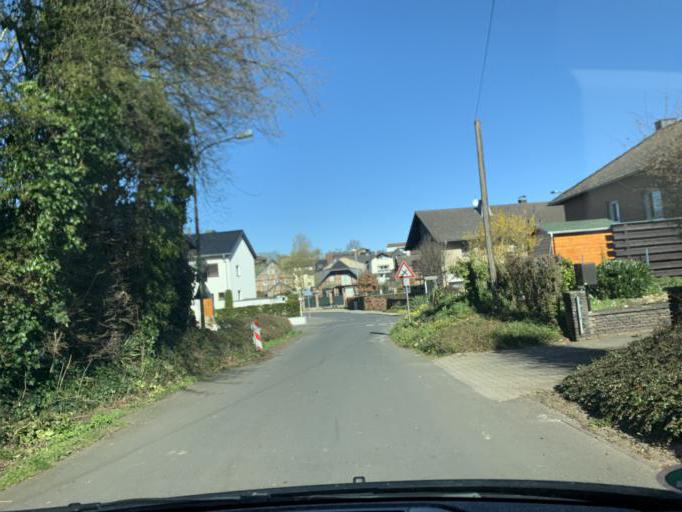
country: DE
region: North Rhine-Westphalia
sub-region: Regierungsbezirk Koln
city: Nideggen
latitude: 50.7137
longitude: 6.4986
